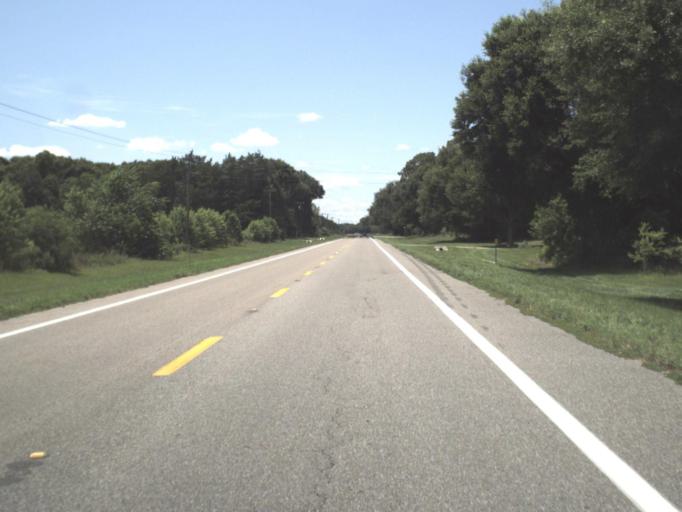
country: US
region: Florida
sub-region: Lafayette County
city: Mayo
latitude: 30.0436
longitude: -83.0767
